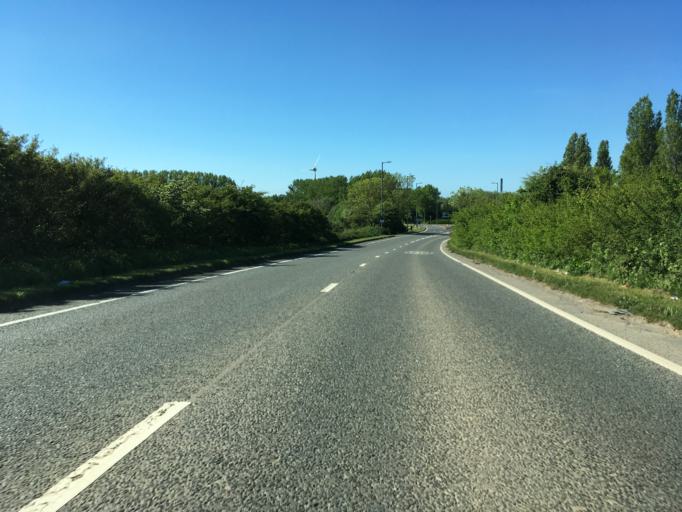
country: GB
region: England
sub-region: South Gloucestershire
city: Severn Beach
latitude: 51.5570
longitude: -2.6539
